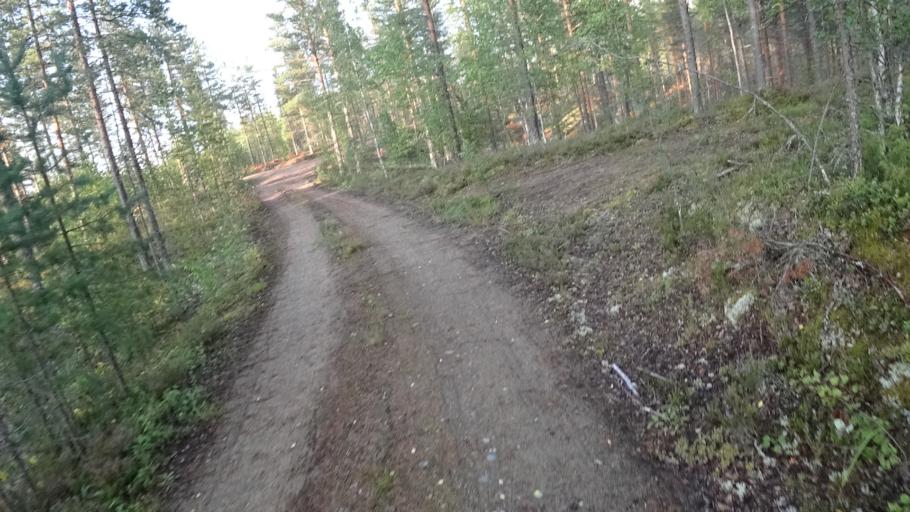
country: FI
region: North Karelia
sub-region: Joensuu
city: Ilomantsi
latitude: 62.6324
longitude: 31.0892
